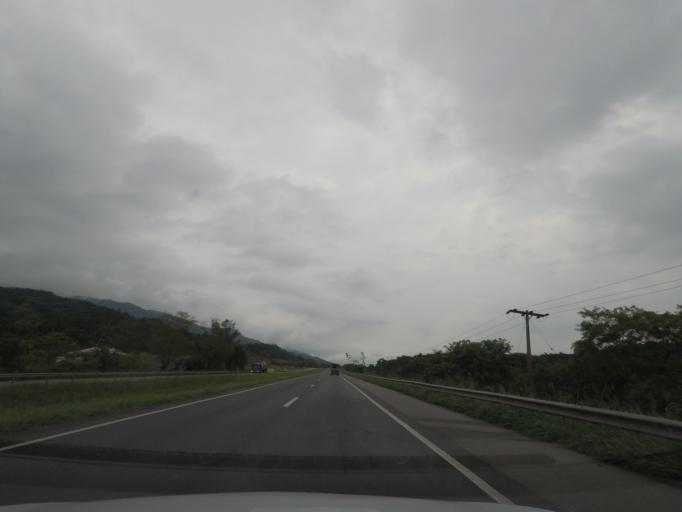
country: BR
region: Sao Paulo
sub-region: Miracatu
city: Miracatu
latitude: -24.2766
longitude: -47.4159
